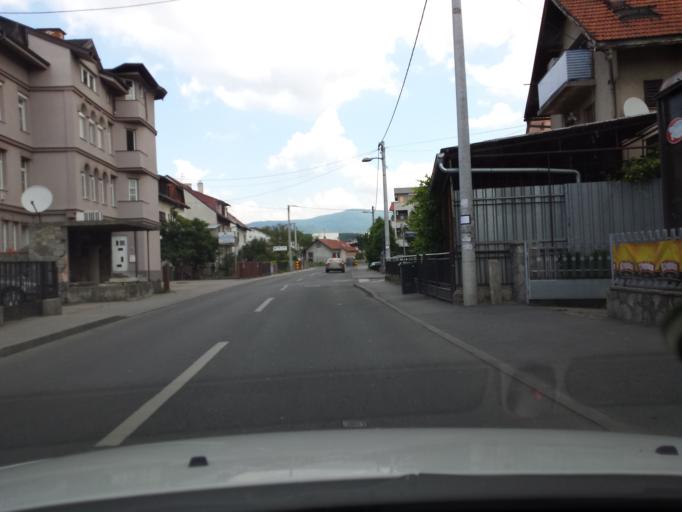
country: HR
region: Grad Zagreb
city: Jankomir
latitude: 45.8000
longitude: 15.9199
